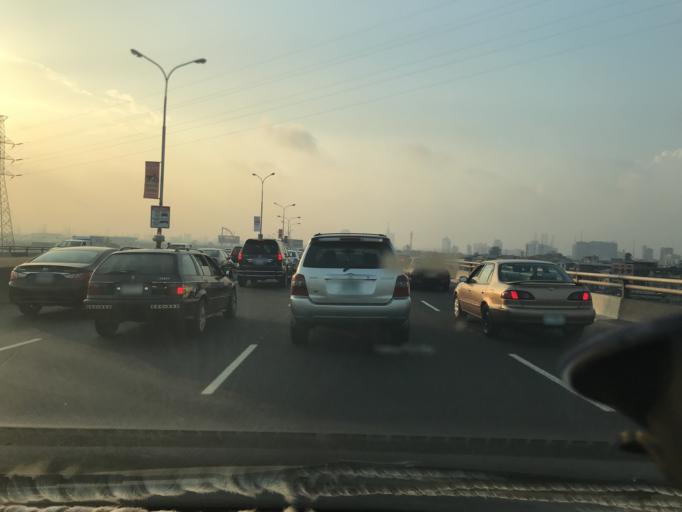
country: NG
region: Lagos
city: Lagos
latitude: 6.4675
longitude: 3.3913
